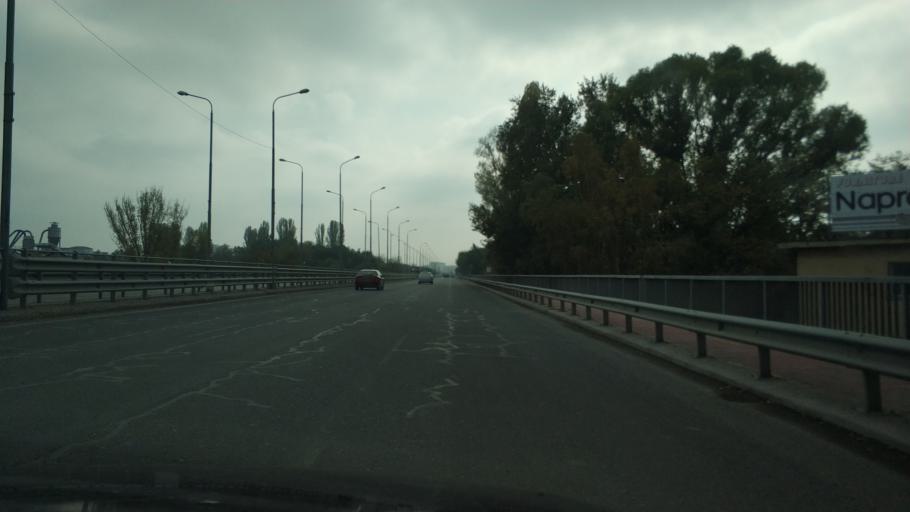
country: BG
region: Plovdiv
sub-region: Obshtina Plovdiv
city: Plovdiv
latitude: 42.1588
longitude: 24.7649
